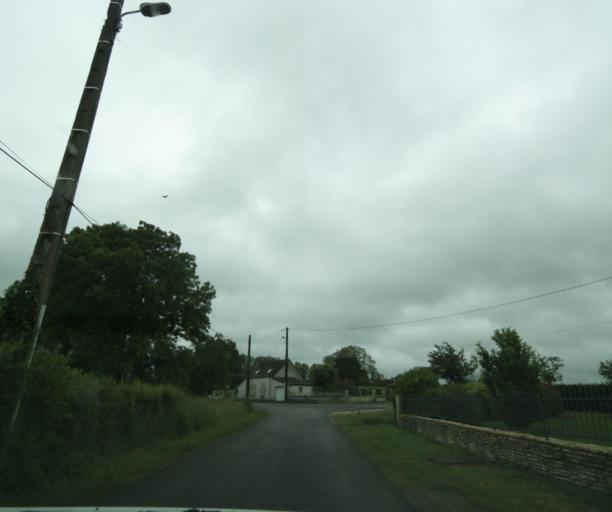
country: FR
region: Bourgogne
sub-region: Departement de Saone-et-Loire
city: Palinges
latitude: 46.5664
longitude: 4.2168
